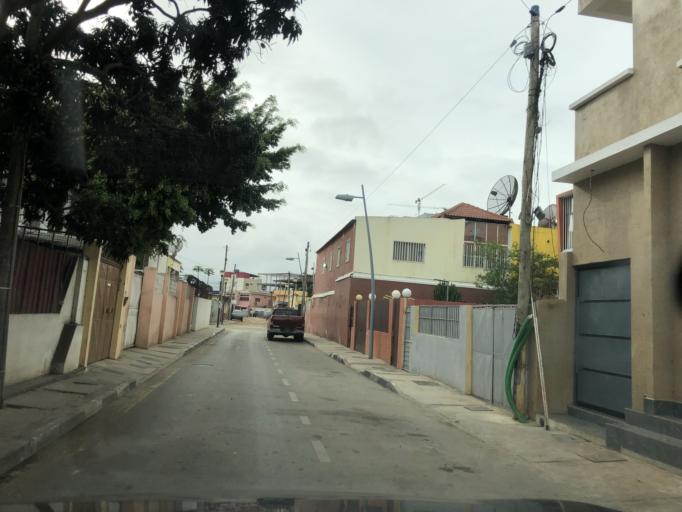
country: AO
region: Luanda
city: Luanda
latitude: -8.8216
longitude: 13.2514
